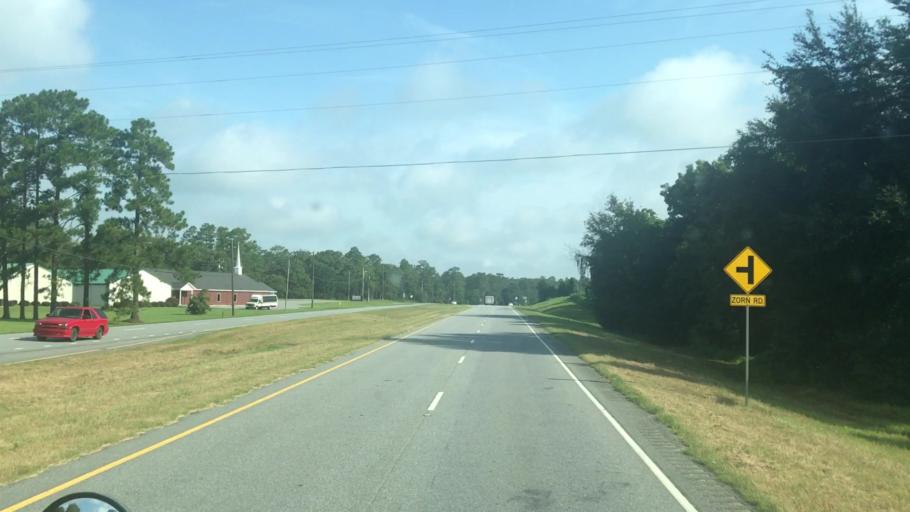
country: US
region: Georgia
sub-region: Decatur County
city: Bainbridge
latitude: 30.9447
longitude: -84.6107
